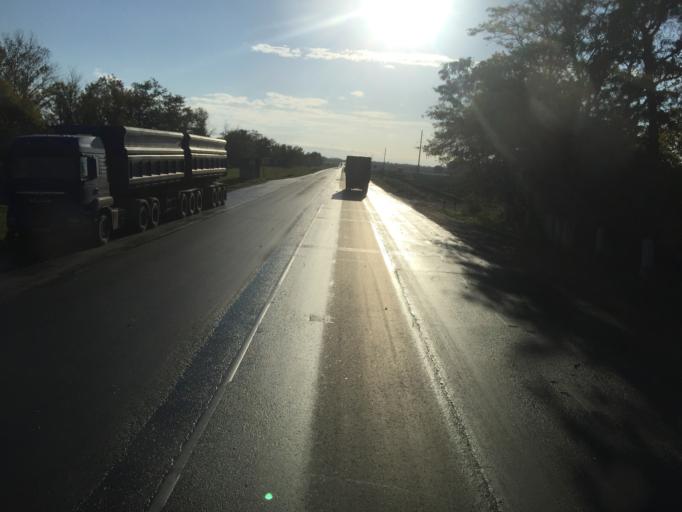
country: RU
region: Rostov
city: Mechetinskaya
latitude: 46.7960
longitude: 40.3773
